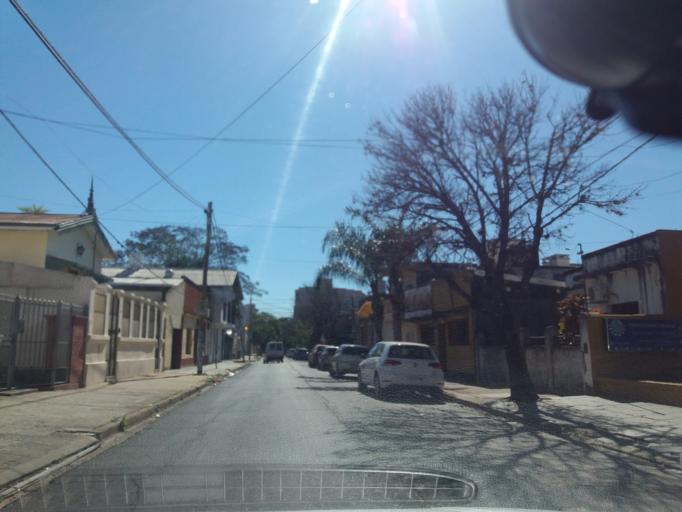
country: AR
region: Corrientes
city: Corrientes
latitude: -27.4720
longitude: -58.8433
